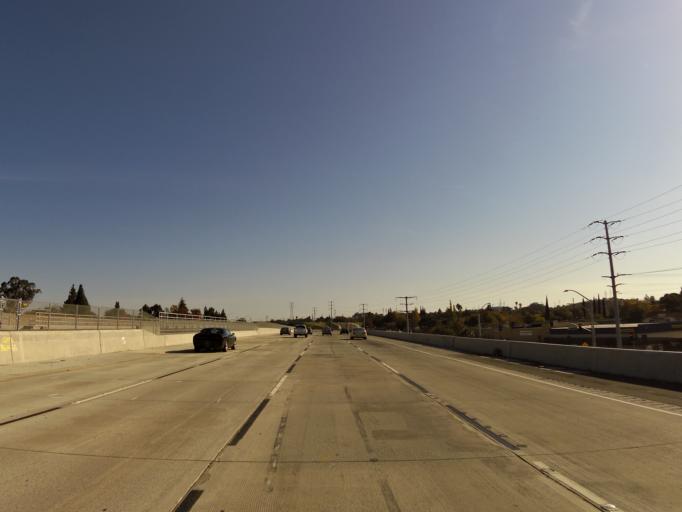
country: US
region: California
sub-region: Contra Costa County
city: Antioch
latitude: 37.9998
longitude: -121.8224
